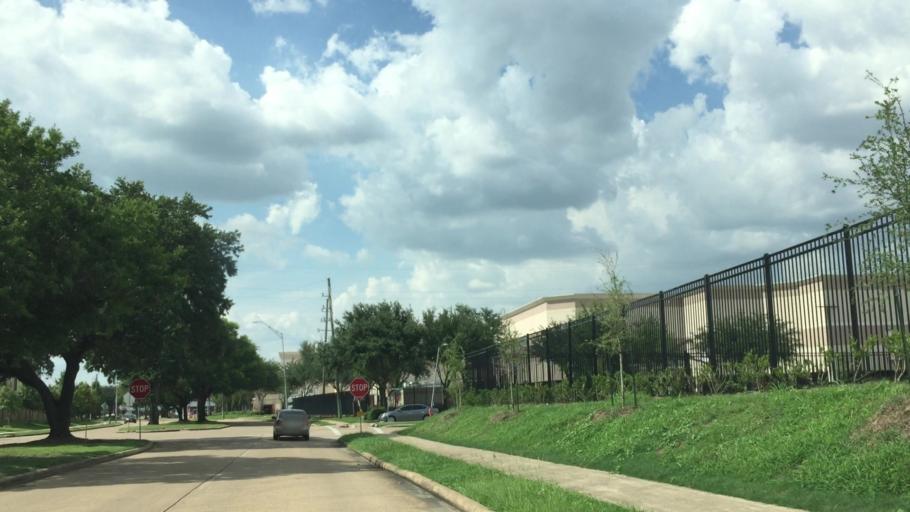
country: US
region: Texas
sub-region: Harris County
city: Bunker Hill Village
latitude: 29.7332
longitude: -95.5953
